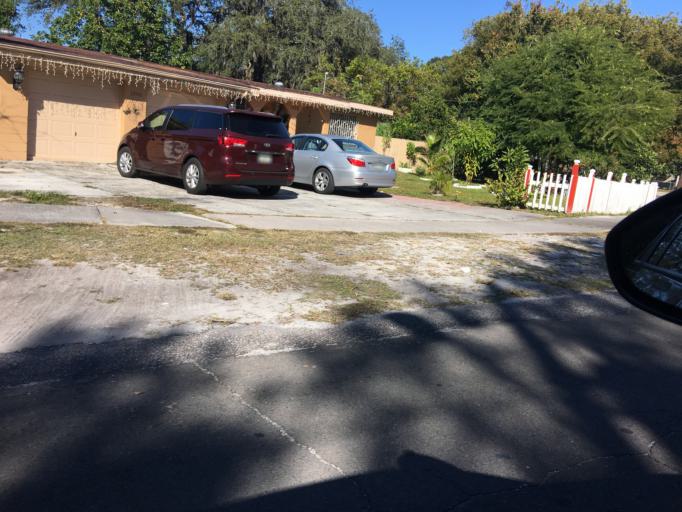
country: US
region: Florida
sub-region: Hillsborough County
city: University
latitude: 28.0395
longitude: -82.4383
